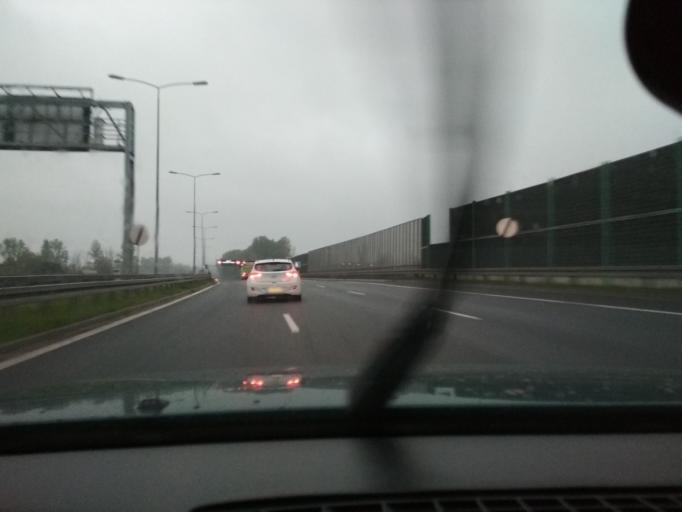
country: PL
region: Silesian Voivodeship
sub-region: Powiat gliwicki
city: Przyszowice
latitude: 50.2841
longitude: 18.7431
